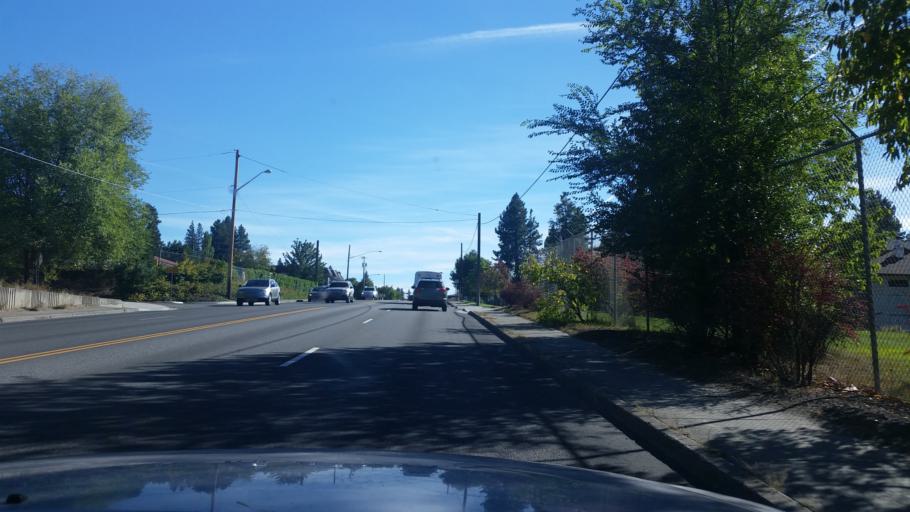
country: US
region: Washington
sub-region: Spokane County
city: Spokane
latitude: 47.6324
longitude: -117.3632
